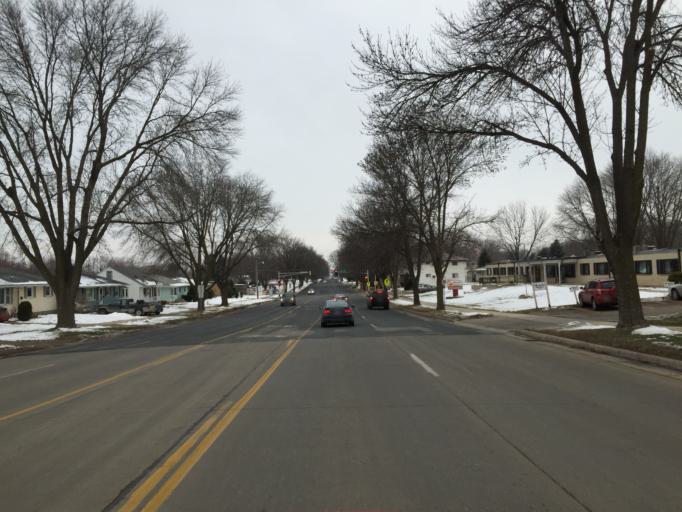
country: US
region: Minnesota
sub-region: Olmsted County
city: Rochester
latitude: 44.0435
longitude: -92.4909
